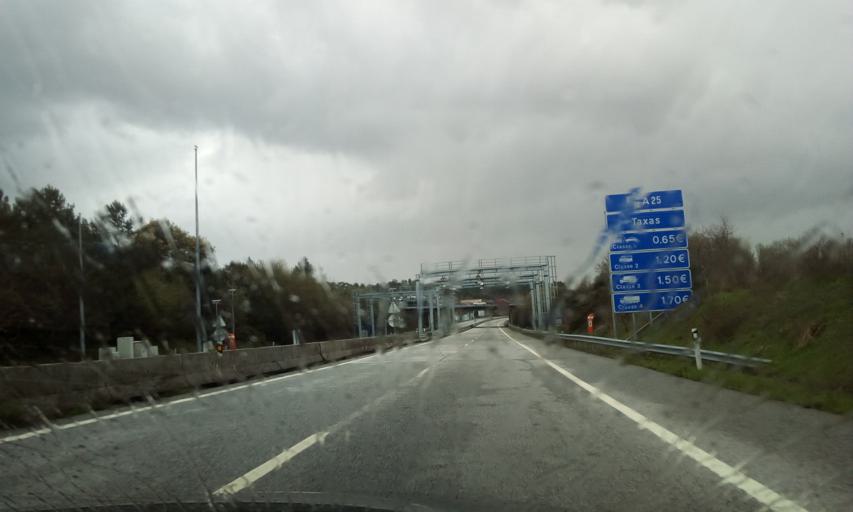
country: PT
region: Viseu
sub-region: Viseu
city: Rio de Loba
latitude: 40.6484
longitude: -7.8689
